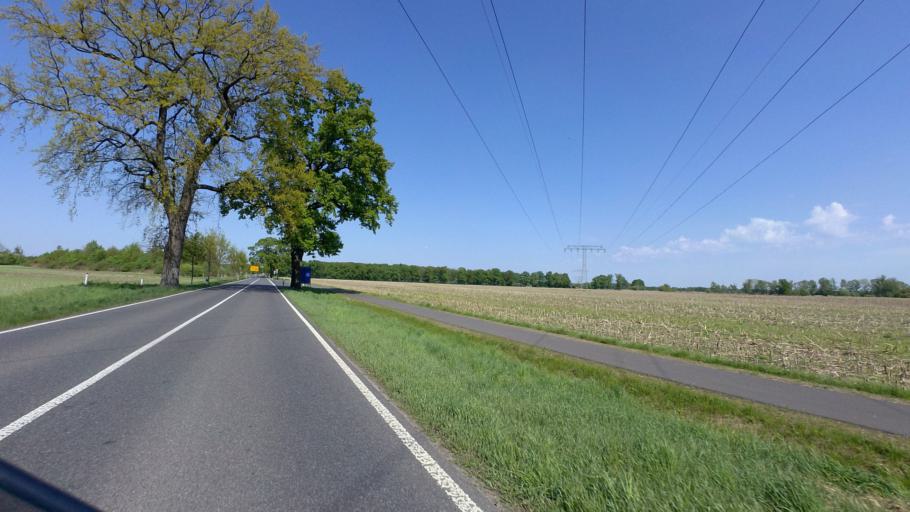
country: DE
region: Brandenburg
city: Beeskow
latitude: 52.1879
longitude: 14.2885
